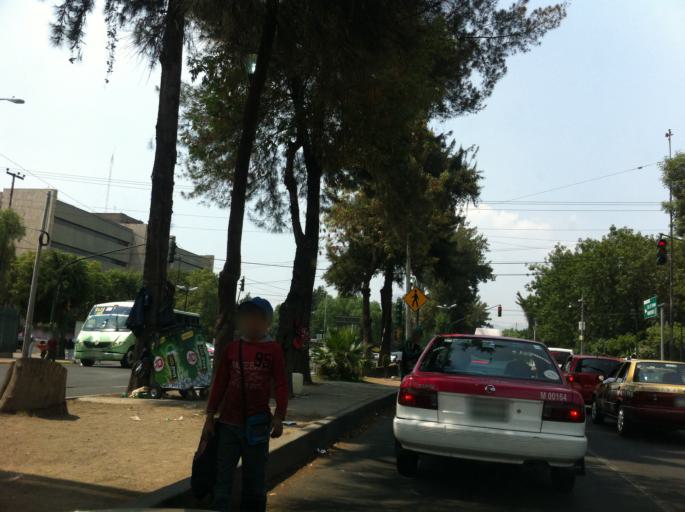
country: MX
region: Mexico
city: Colonia Lindavista
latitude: 19.4835
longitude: -99.1348
